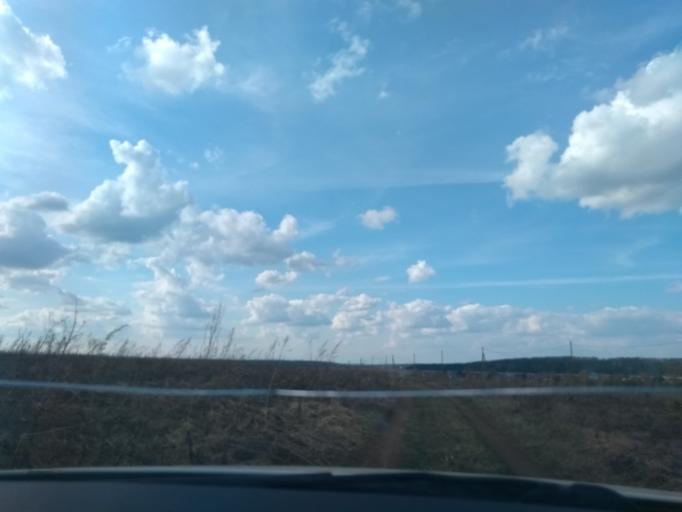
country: RU
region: Perm
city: Sylva
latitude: 57.8421
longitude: 56.7910
